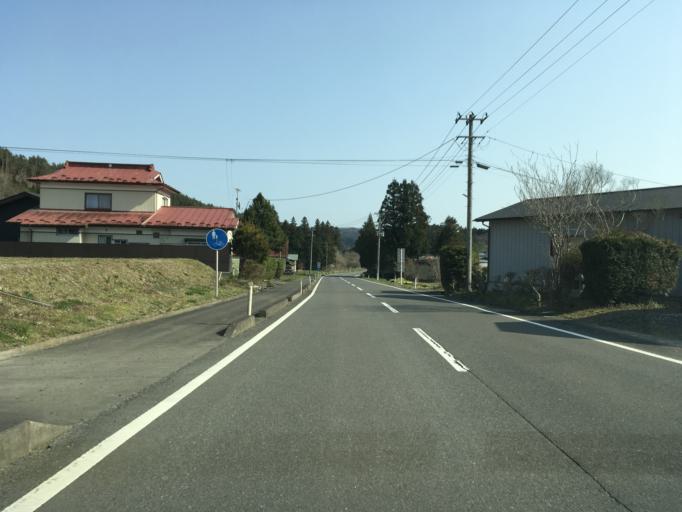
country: JP
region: Iwate
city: Ichinoseki
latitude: 38.7895
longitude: 141.3226
